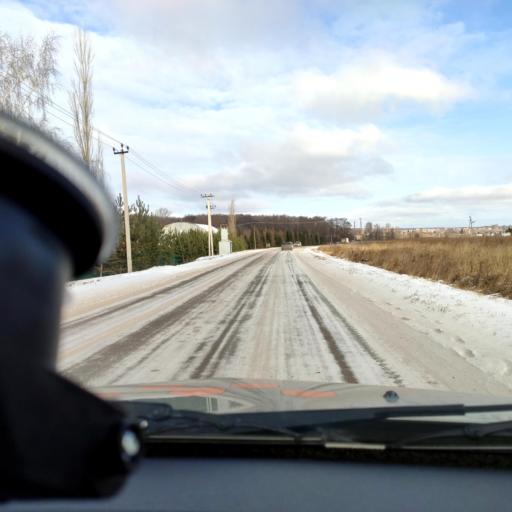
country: RU
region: Bashkortostan
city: Avdon
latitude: 54.7885
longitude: 55.7611
